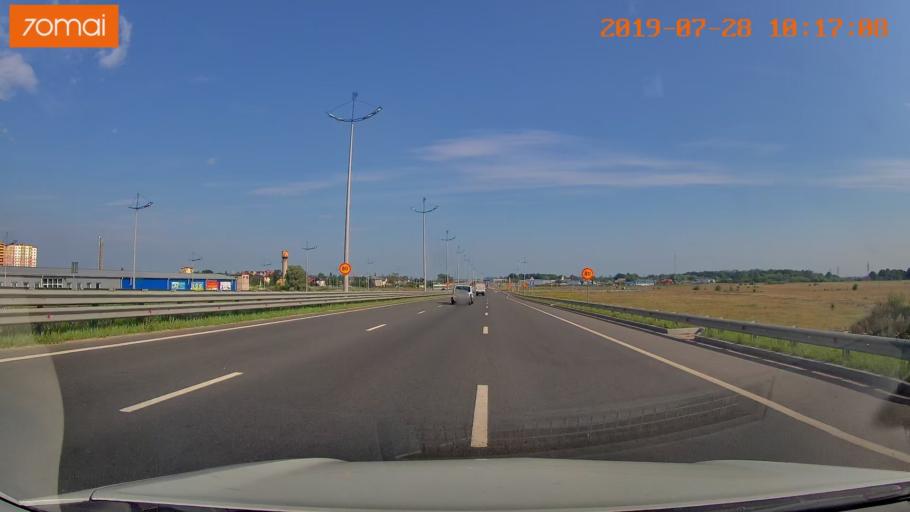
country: RU
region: Kaliningrad
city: Maloye Isakovo
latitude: 54.7360
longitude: 20.5962
